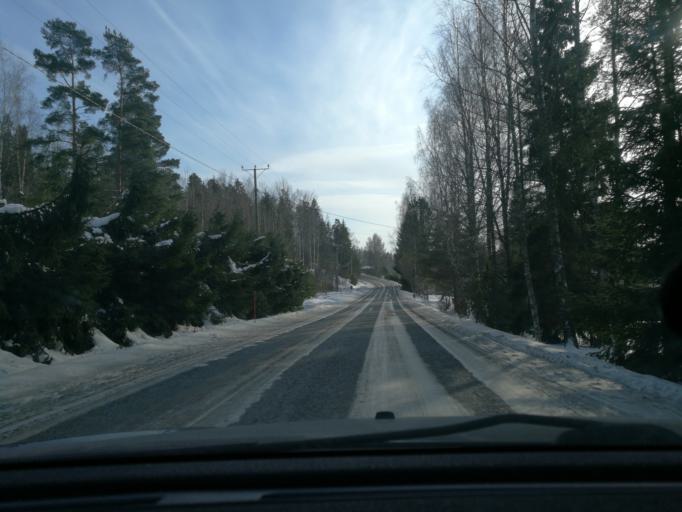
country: FI
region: Uusimaa
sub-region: Helsinki
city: Saukkola
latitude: 60.4640
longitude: 23.9897
